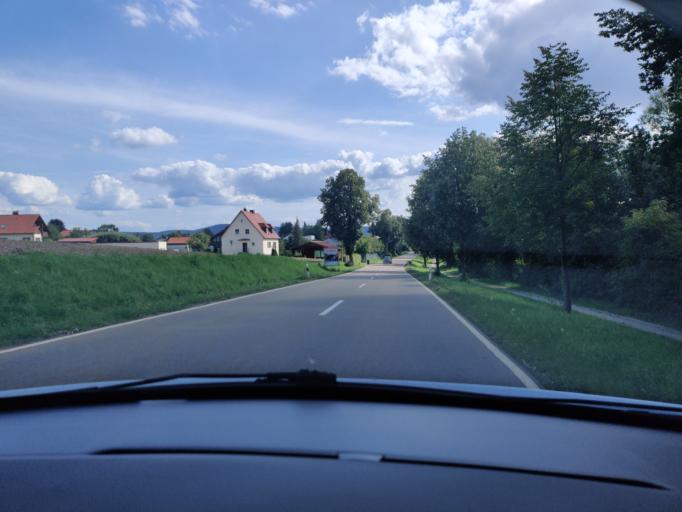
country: DE
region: Bavaria
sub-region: Upper Palatinate
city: Nabburg
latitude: 49.4651
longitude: 12.1866
